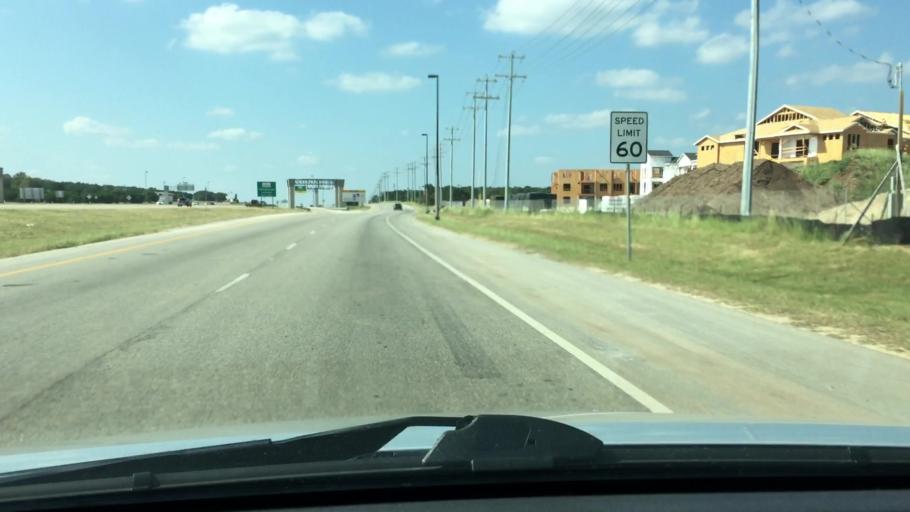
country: US
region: Texas
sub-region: Williamson County
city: Leander
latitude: 30.5666
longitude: -97.8262
